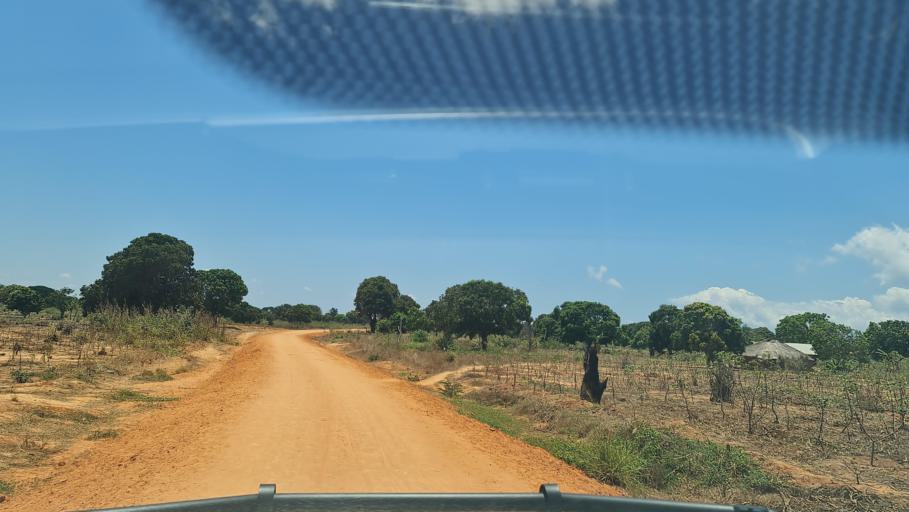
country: MZ
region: Nampula
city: Nacala
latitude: -14.2236
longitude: 40.6857
